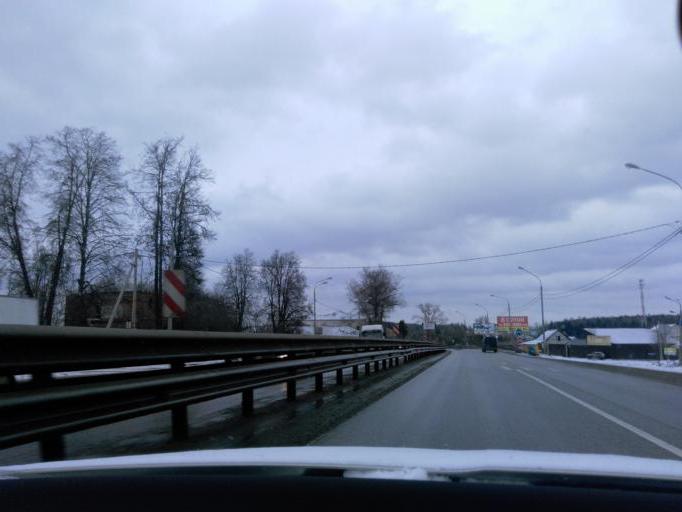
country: RU
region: Moskovskaya
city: Skhodnya
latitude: 55.9761
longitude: 37.3049
